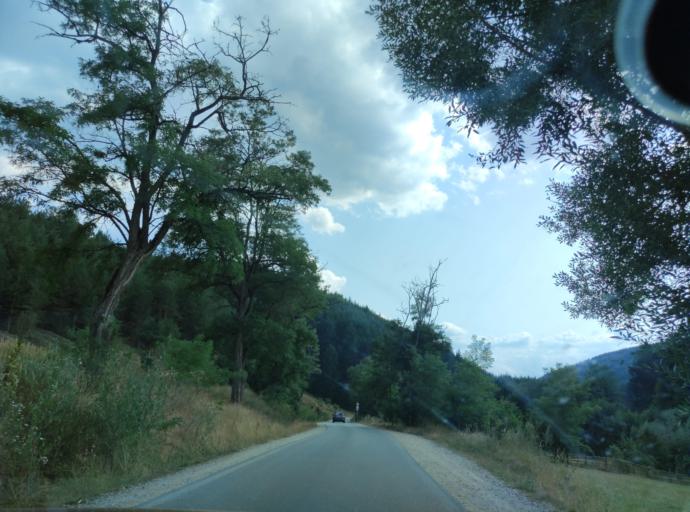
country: BG
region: Blagoevgrad
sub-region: Obshtina Belitsa
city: Belitsa
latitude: 41.9701
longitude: 23.5560
